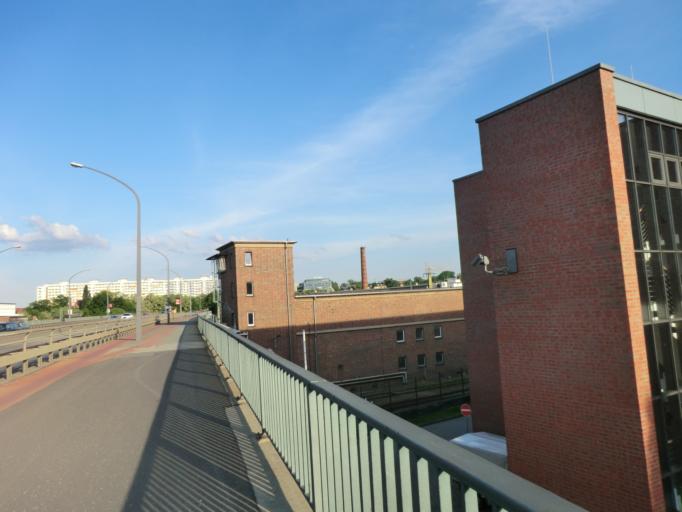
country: DE
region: Saxony
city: Dresden
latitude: 51.0402
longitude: 13.7102
